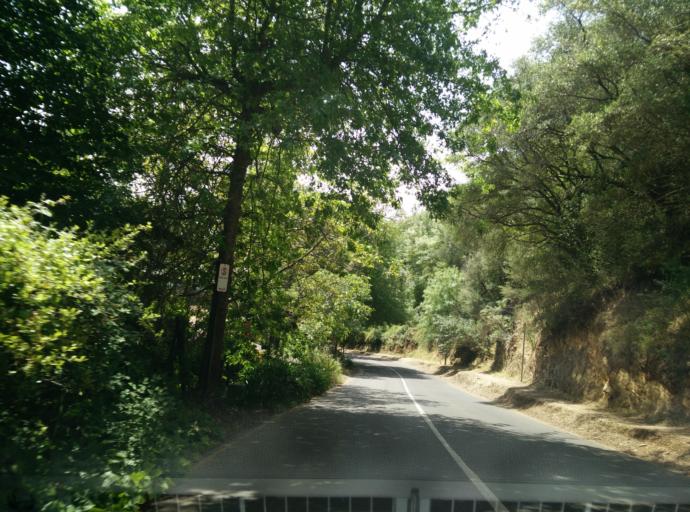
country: AU
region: South Australia
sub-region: Burnside
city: Mount Osmond
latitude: -34.9672
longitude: 138.6797
